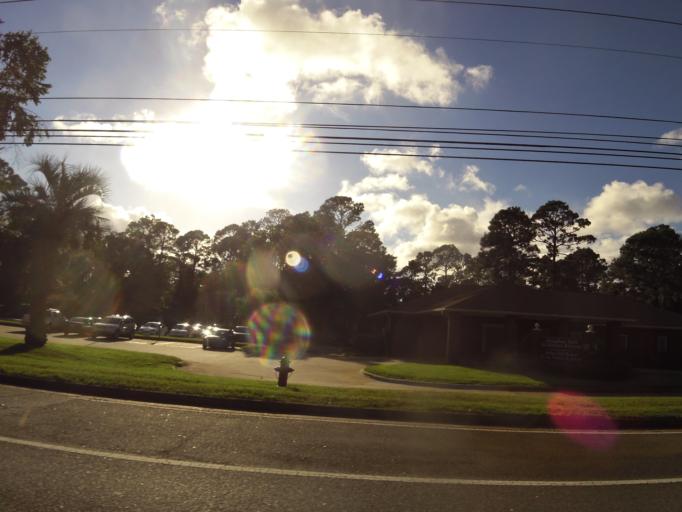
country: US
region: Georgia
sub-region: Glynn County
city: Country Club Estates
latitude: 31.2003
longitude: -81.4842
